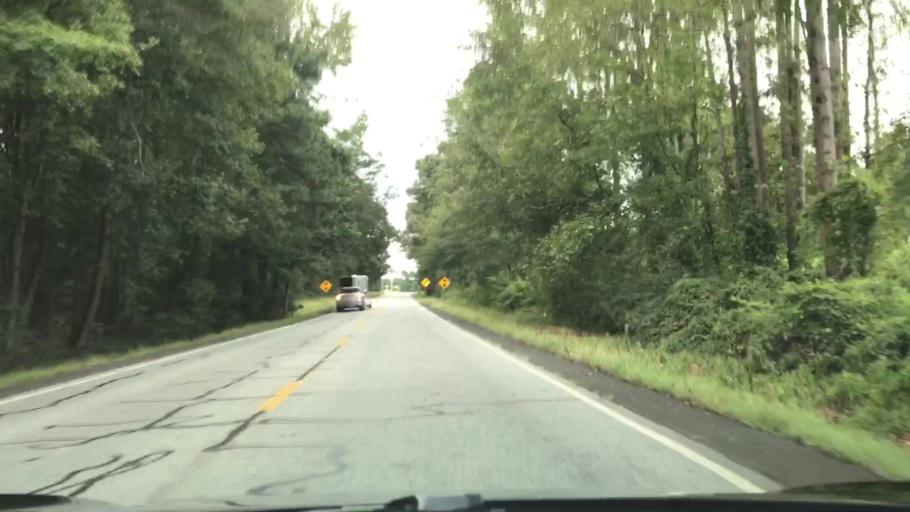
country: US
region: Georgia
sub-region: Barrow County
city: Russell
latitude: 33.9579
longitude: -83.6599
